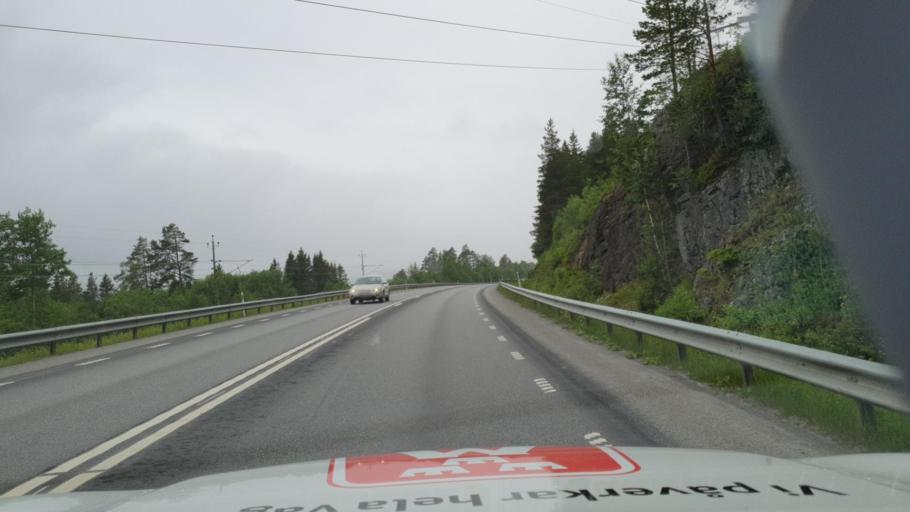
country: SE
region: Jaemtland
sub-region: Are Kommun
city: Jarpen
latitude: 63.3087
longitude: 13.6221
